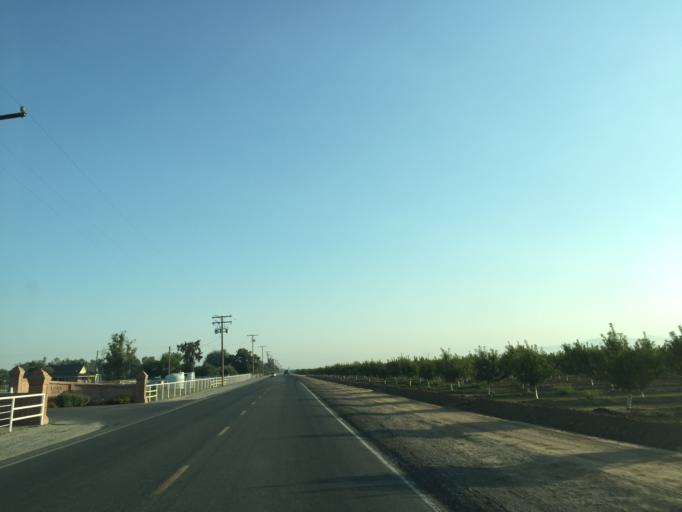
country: US
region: California
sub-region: Tulare County
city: Ivanhoe
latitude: 36.4193
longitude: -119.2780
